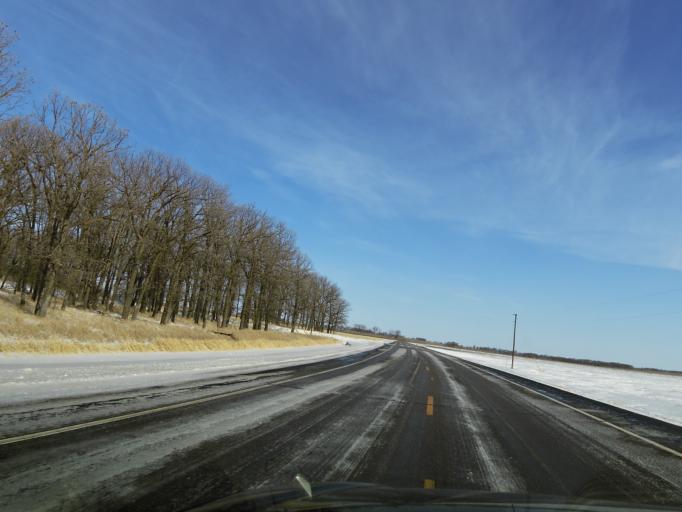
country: US
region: North Dakota
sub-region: Walsh County
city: Grafton
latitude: 48.4138
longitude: -97.1261
